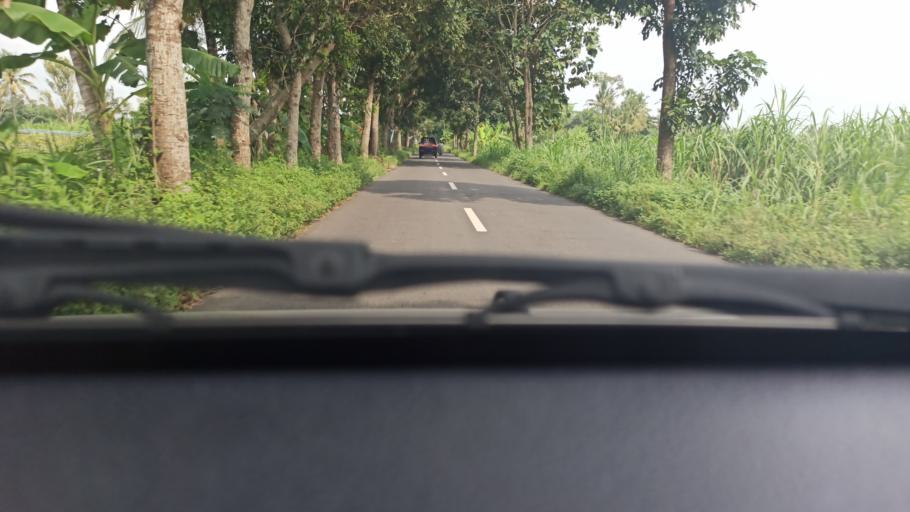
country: ID
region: Daerah Istimewa Yogyakarta
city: Sleman
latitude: -7.6919
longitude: 110.2987
